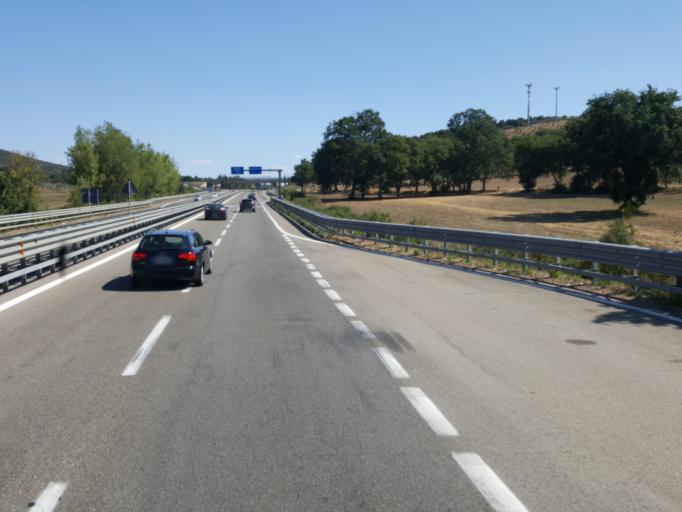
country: IT
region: Tuscany
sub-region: Provincia di Grosseto
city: Campagnatico
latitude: 42.8689
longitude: 11.2031
